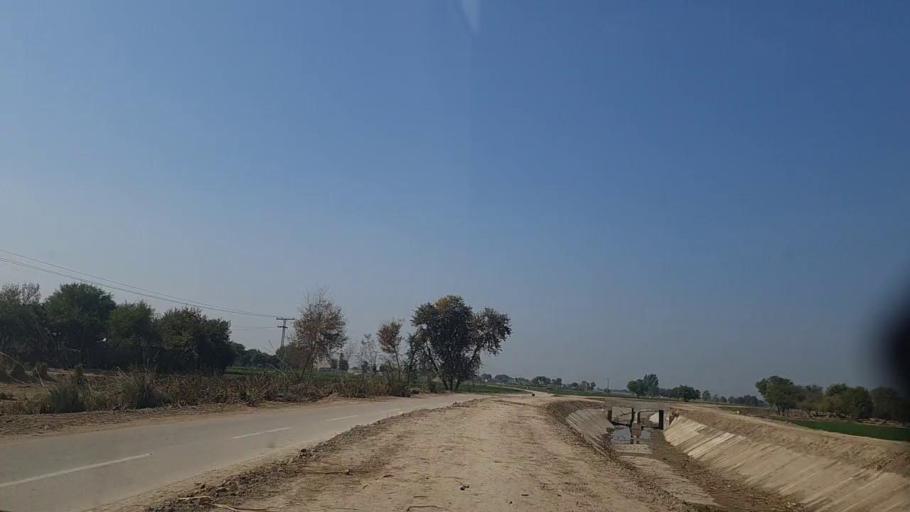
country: PK
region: Sindh
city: Sakrand
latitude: 26.1462
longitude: 68.3359
